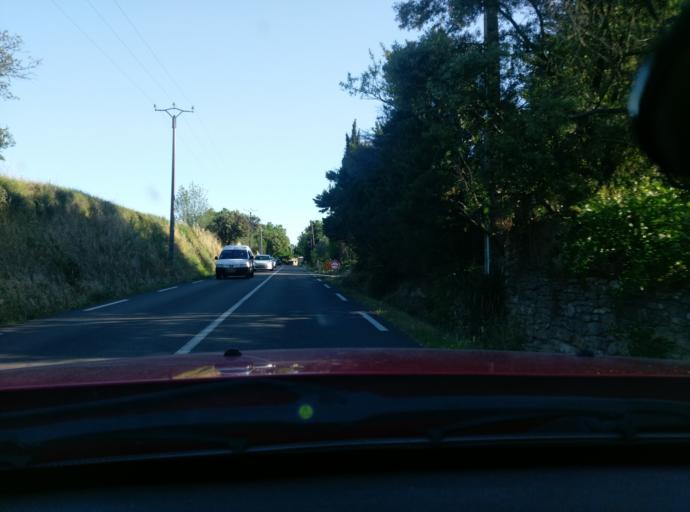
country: FR
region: Languedoc-Roussillon
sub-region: Departement du Gard
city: Remoulins
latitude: 43.9298
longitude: 4.5602
